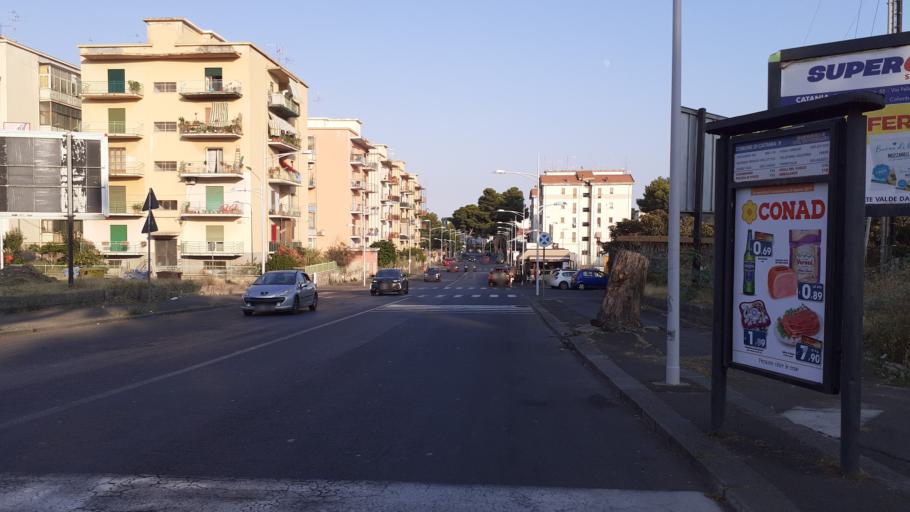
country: IT
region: Sicily
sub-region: Catania
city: Catania
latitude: 37.5043
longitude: 15.0559
